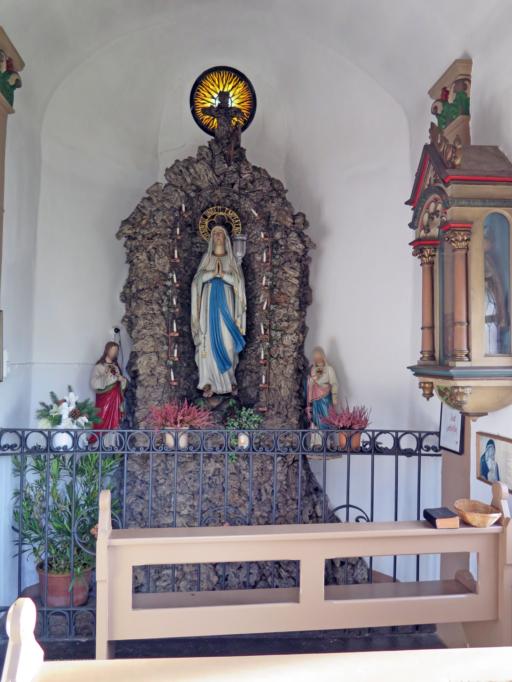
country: DE
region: Bavaria
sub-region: Regierungsbezirk Unterfranken
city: Hassfurt
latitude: 50.0301
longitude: 10.5173
